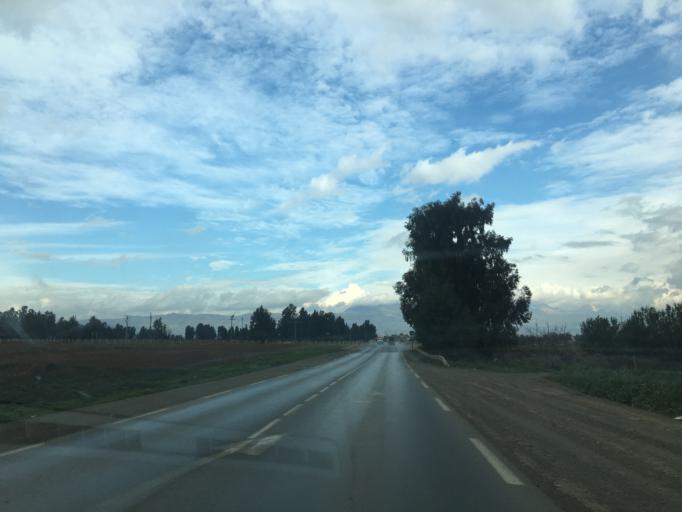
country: DZ
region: Bouira
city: Bouira
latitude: 36.3583
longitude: 3.8471
